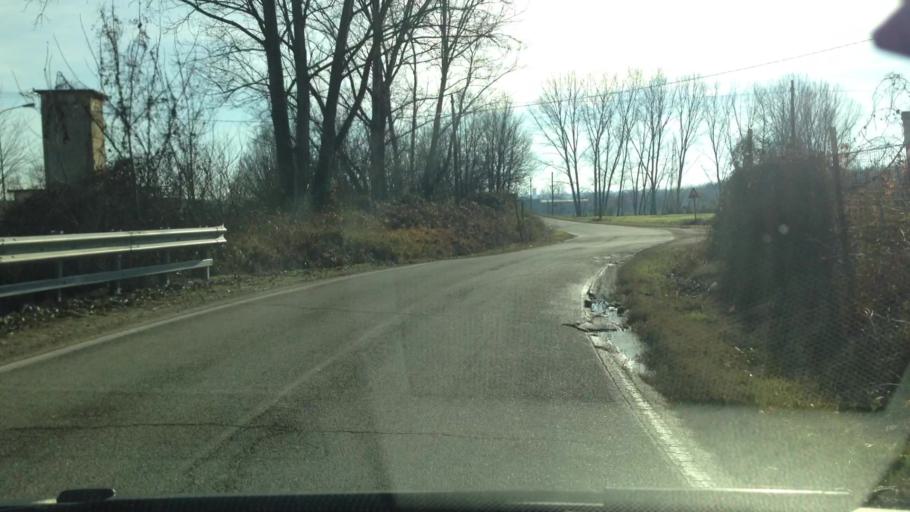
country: IT
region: Piedmont
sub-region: Provincia di Alessandria
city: Quattordio
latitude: 44.8920
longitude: 8.4044
